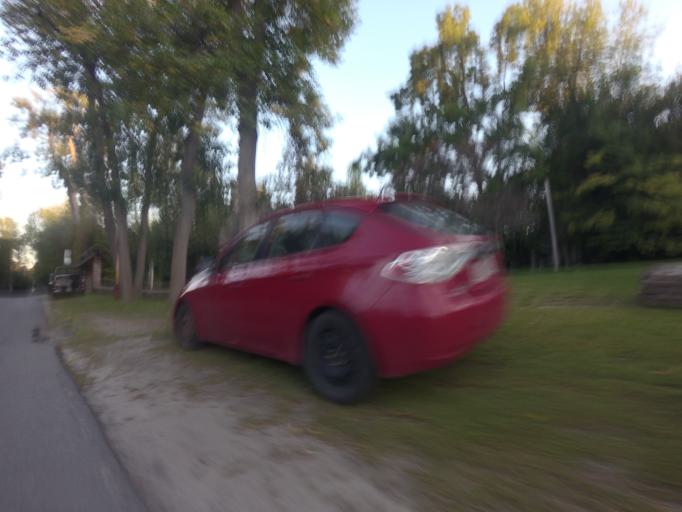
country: CA
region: Quebec
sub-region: Laurentides
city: Oka
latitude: 45.4520
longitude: -74.1148
